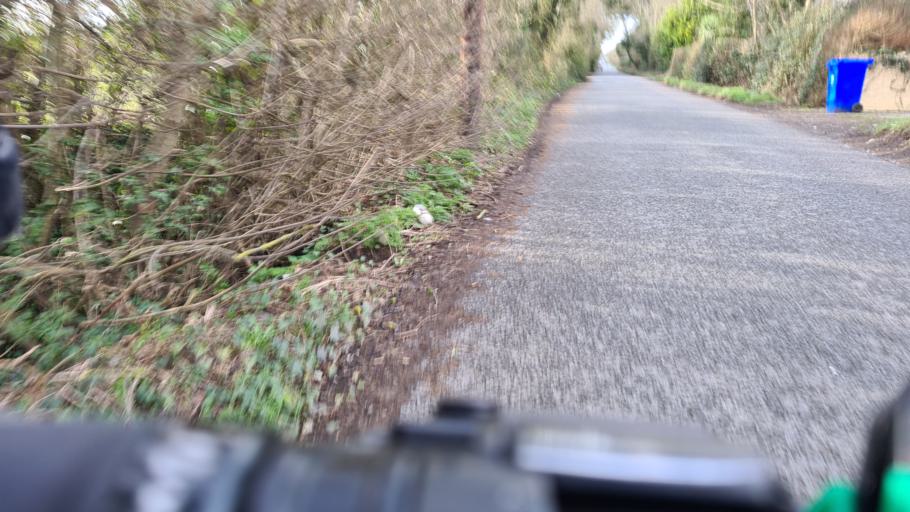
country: IE
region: Leinster
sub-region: Kildare
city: Celbridge
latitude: 53.3433
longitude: -6.5603
